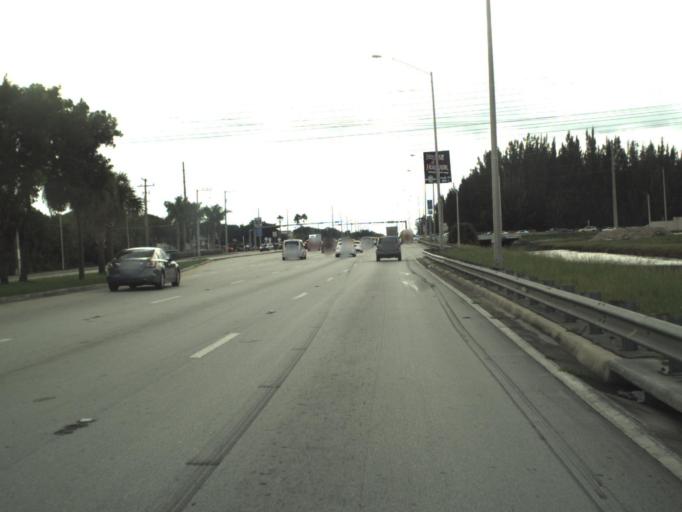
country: US
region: Florida
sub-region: Miami-Dade County
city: Tamiami
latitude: 25.7611
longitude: -80.4145
